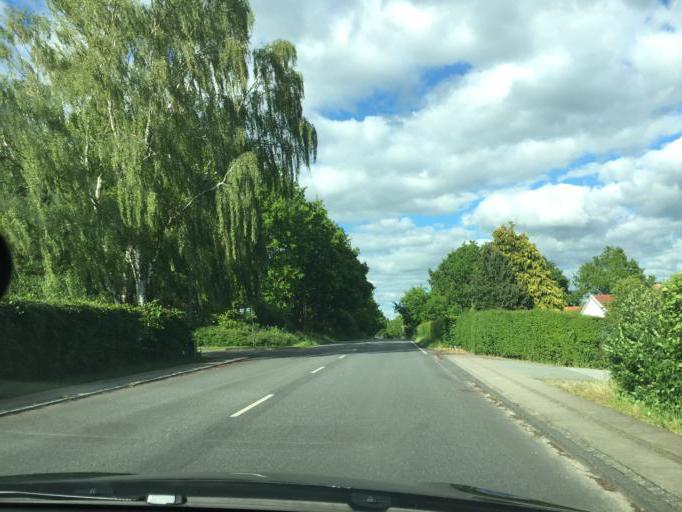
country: DK
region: South Denmark
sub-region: Odense Kommune
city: Bellinge
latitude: 55.3394
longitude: 10.3179
